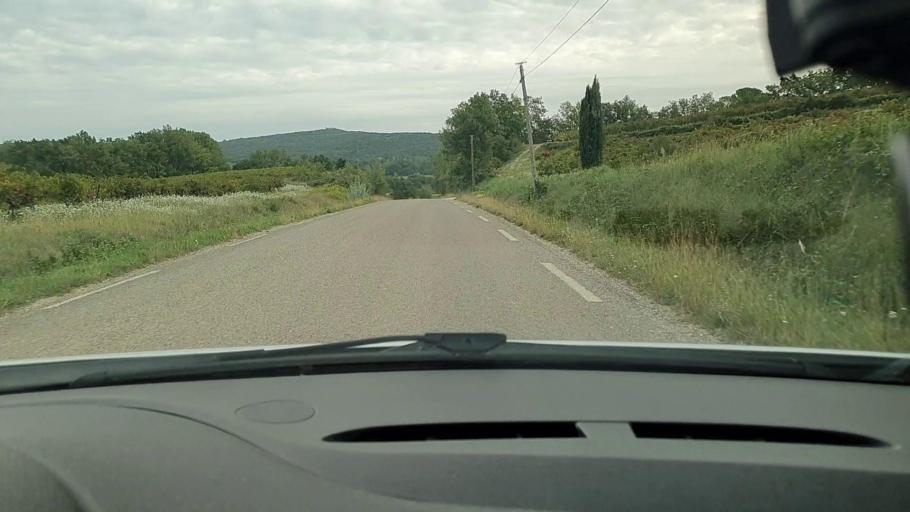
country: FR
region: Languedoc-Roussillon
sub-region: Departement du Gard
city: Moussac
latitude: 44.0330
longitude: 4.2460
